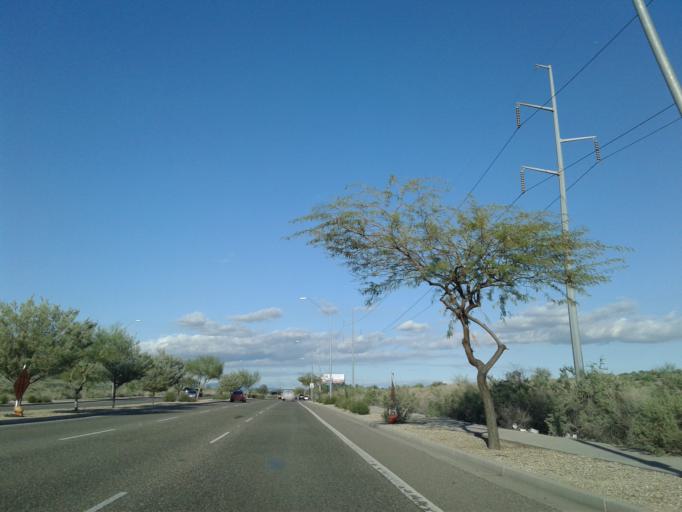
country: US
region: Arizona
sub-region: Maricopa County
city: Cave Creek
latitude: 33.6859
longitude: -112.0519
